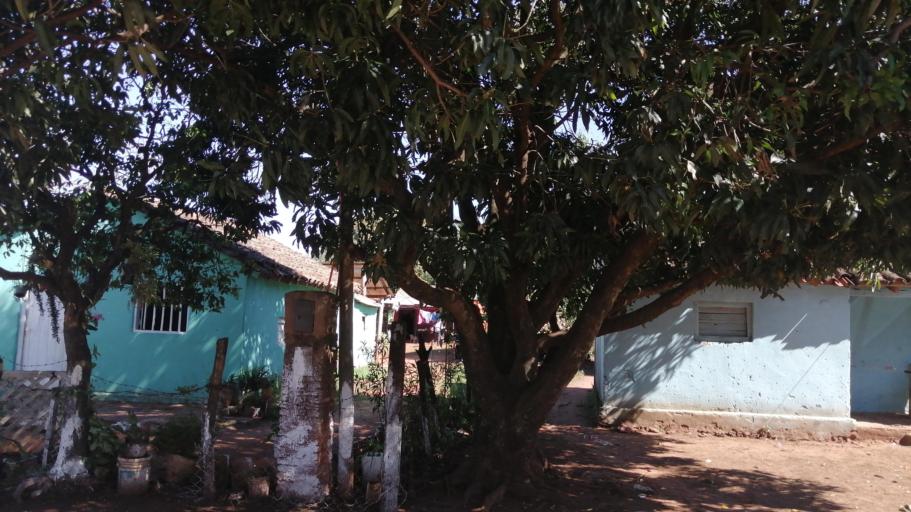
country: PY
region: Misiones
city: San Juan Bautista
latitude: -26.6746
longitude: -57.1427
